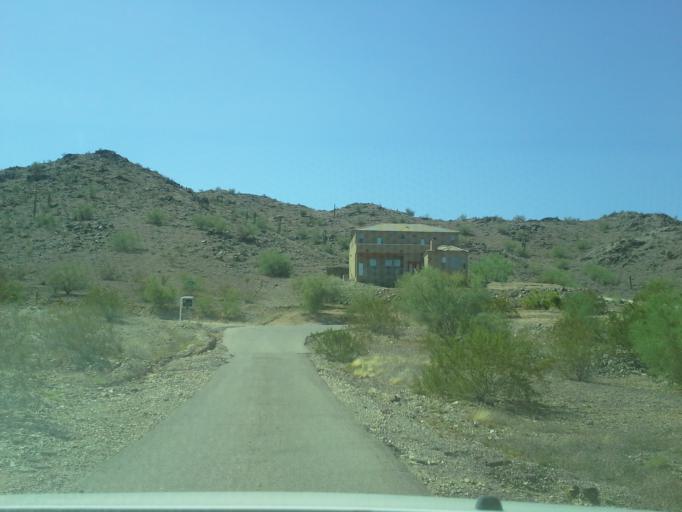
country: US
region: Arizona
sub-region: Maricopa County
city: Laveen
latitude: 33.3491
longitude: -112.1518
